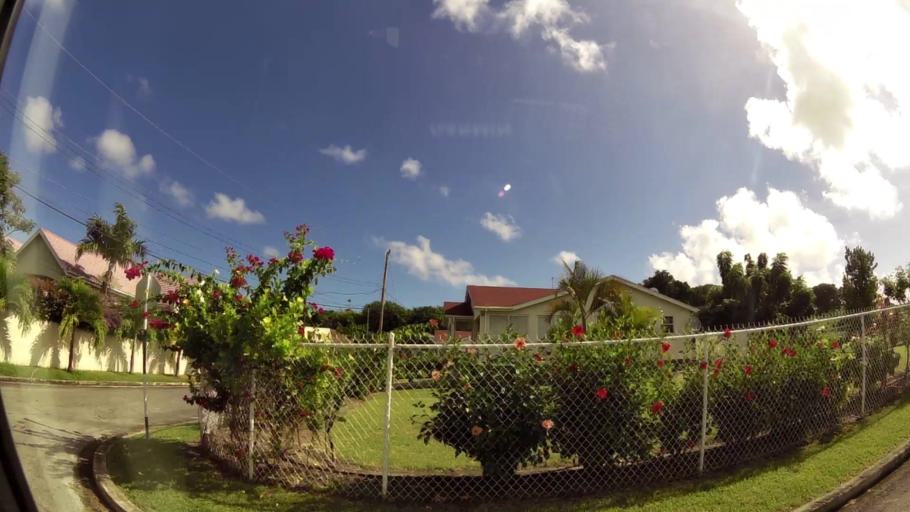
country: BB
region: Saint Lucy
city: Checker Hall
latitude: 13.2731
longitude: -59.6446
